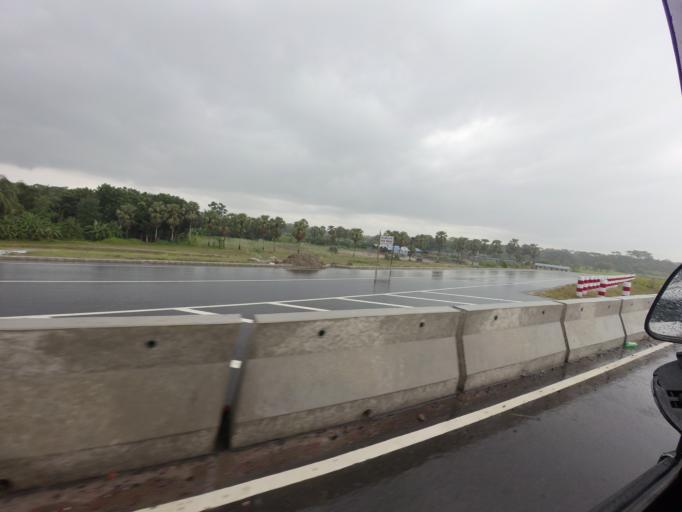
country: BD
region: Dhaka
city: Char Bhadrasan
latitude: 23.3999
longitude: 90.2025
